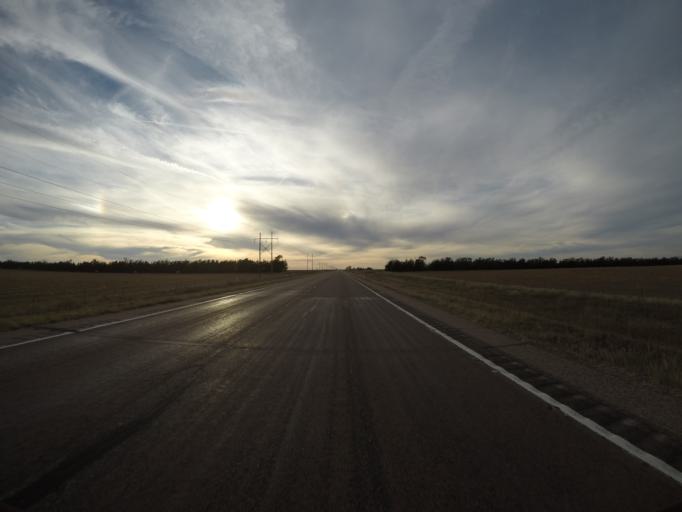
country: US
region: Colorado
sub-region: Yuma County
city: Yuma
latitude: 39.6556
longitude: -102.7522
